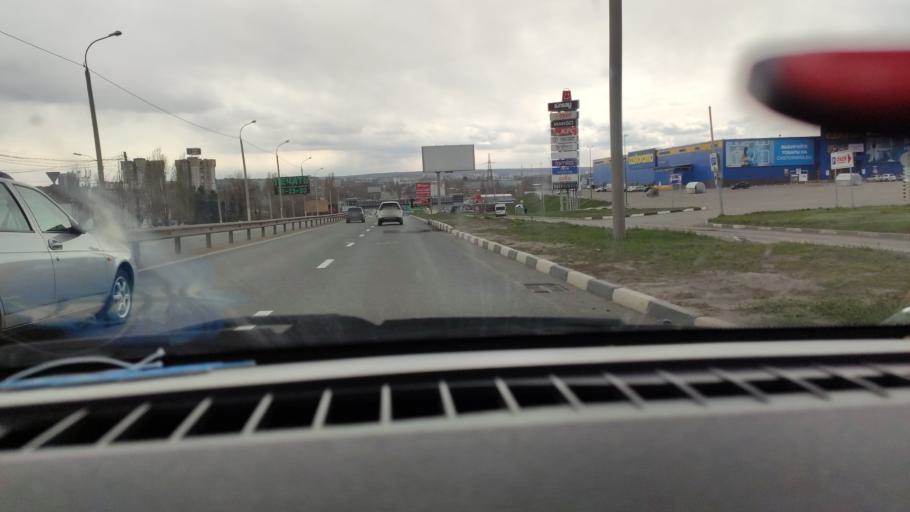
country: RU
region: Saratov
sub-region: Saratovskiy Rayon
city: Saratov
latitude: 51.6187
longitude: 45.9739
